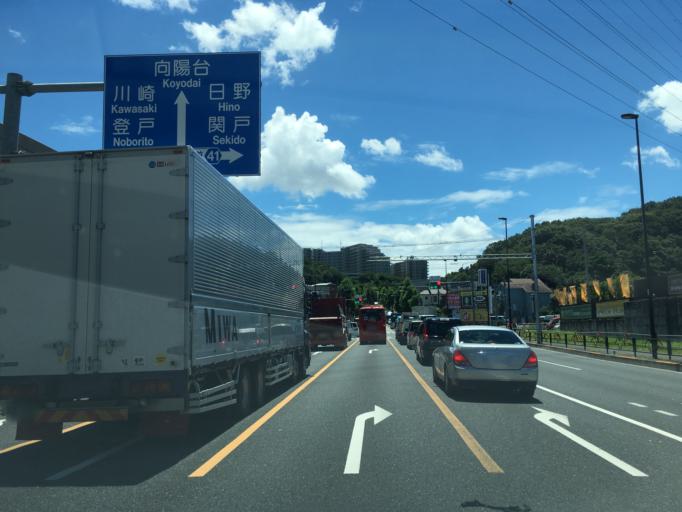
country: JP
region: Tokyo
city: Kokubunji
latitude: 35.6488
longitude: 139.4886
